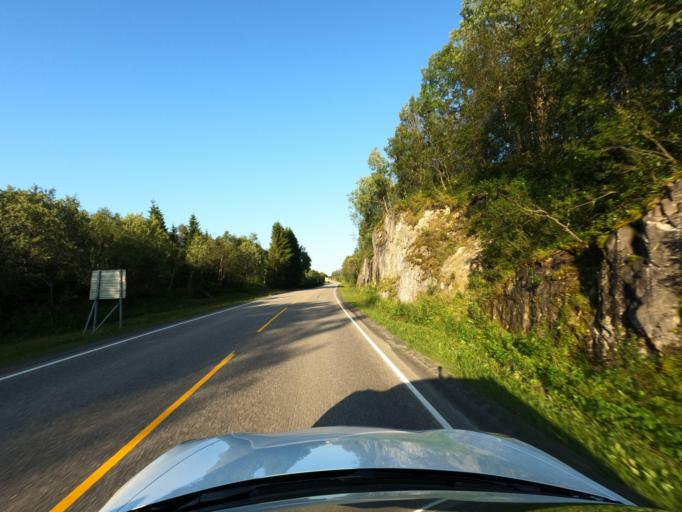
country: NO
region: Troms
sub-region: Skanland
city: Evenskjer
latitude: 68.4926
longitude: 16.7245
